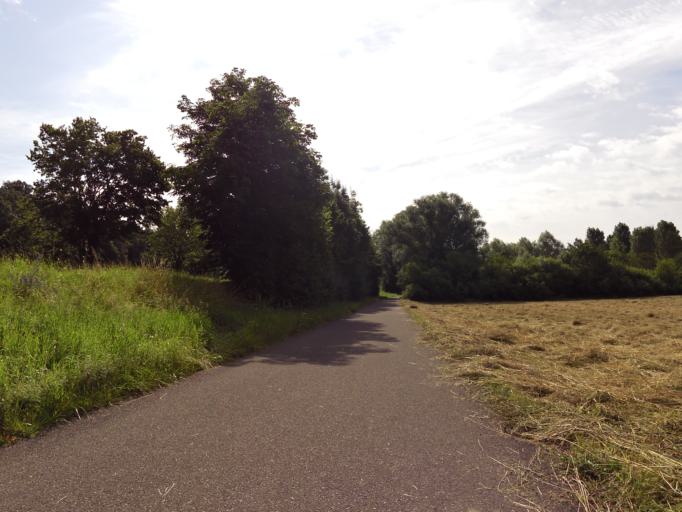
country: DE
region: Baden-Wuerttemberg
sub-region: Freiburg Region
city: Allensbach
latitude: 47.7314
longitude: 9.0226
